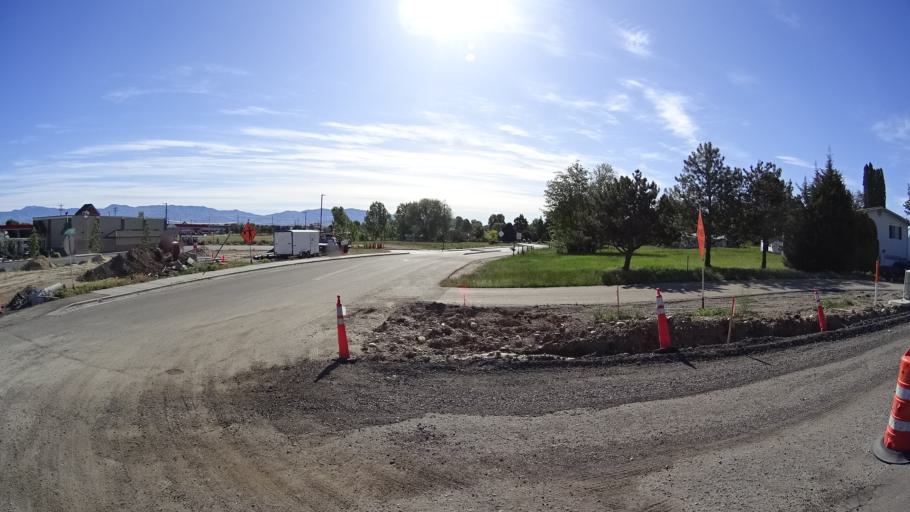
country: US
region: Idaho
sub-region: Ada County
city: Garden City
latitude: 43.5744
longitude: -116.2741
